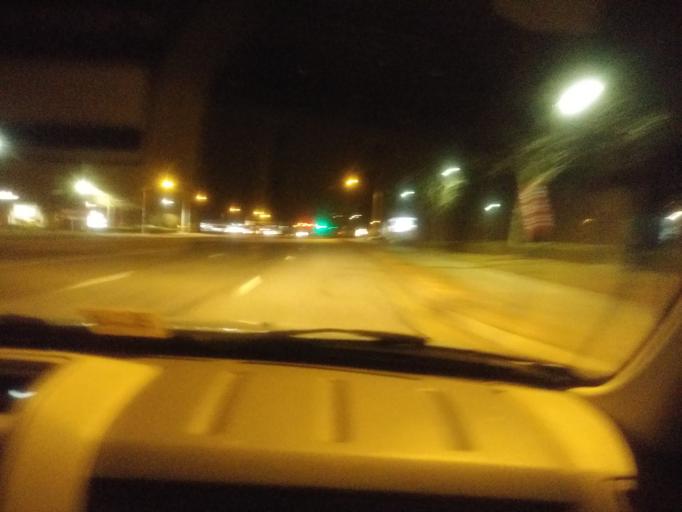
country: US
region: Virginia
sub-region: City of Chesapeake
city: Chesapeake
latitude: 36.7656
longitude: -76.2040
